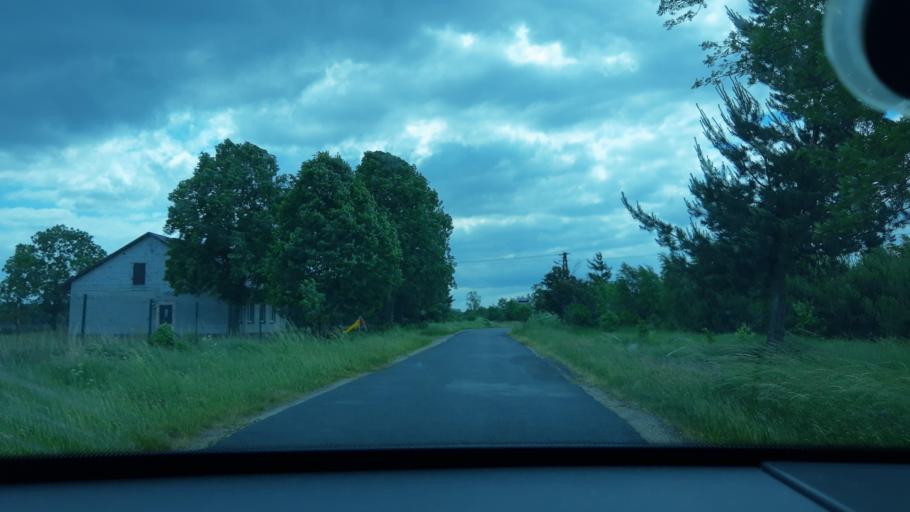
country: PL
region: Lodz Voivodeship
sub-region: Powiat sieradzki
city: Burzenin
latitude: 51.5065
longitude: 18.8471
